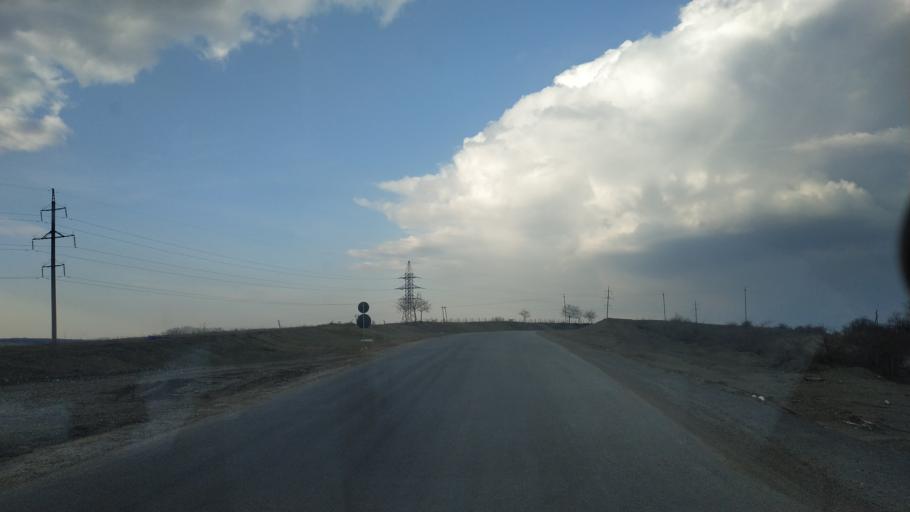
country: MD
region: Anenii Noi
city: Anenii Noi
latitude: 46.9919
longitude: 29.2839
